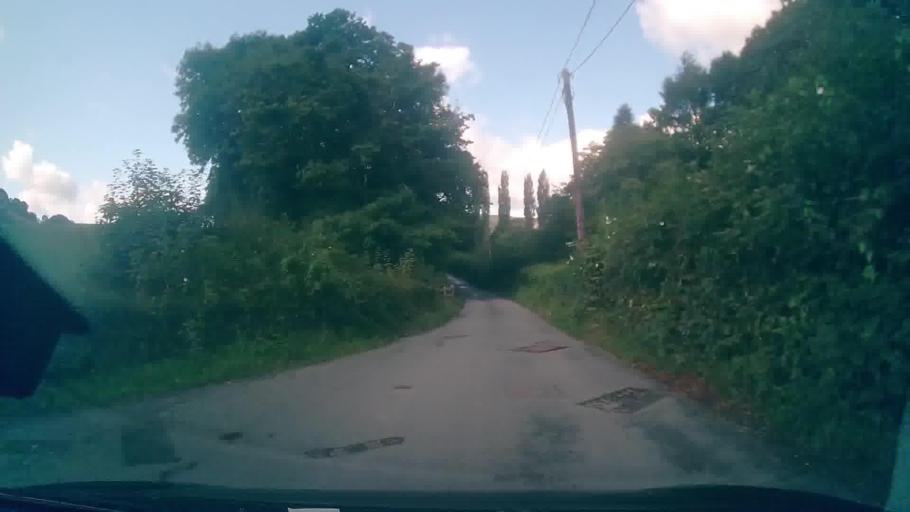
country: GB
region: Wales
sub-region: Sir Powys
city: Llangynog
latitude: 52.8057
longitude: -3.3748
